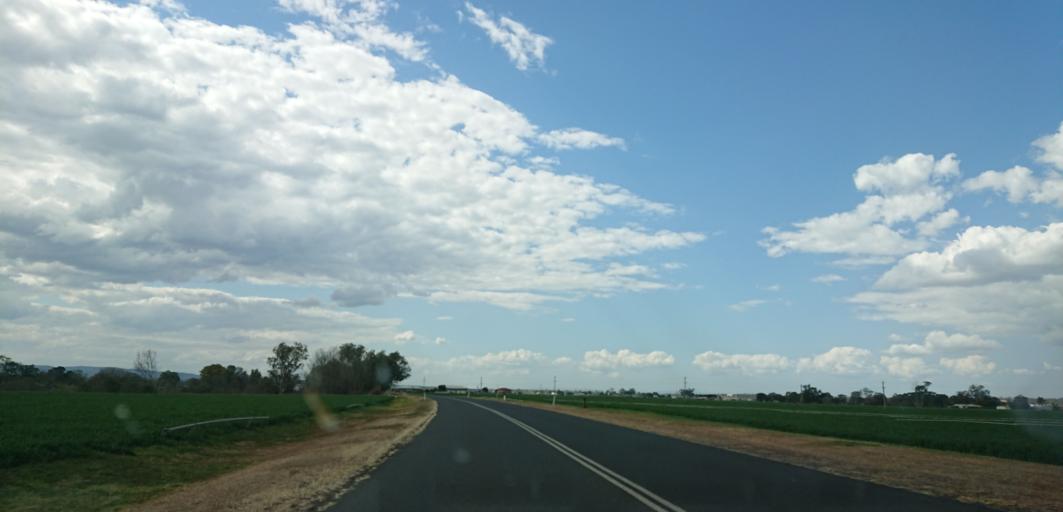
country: AU
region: Queensland
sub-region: Lockyer Valley
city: Gatton
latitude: -27.5963
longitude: 152.2237
